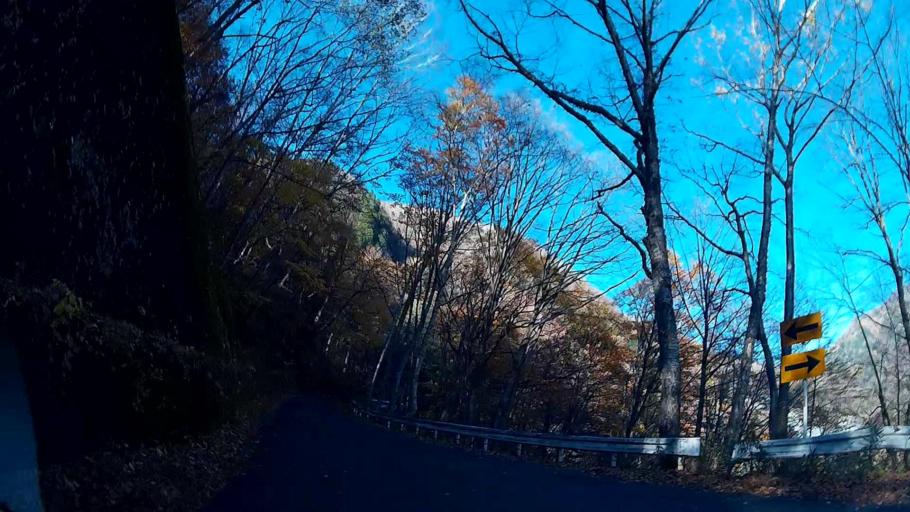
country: JP
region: Nagano
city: Hotaka
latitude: 36.2078
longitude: 137.6031
